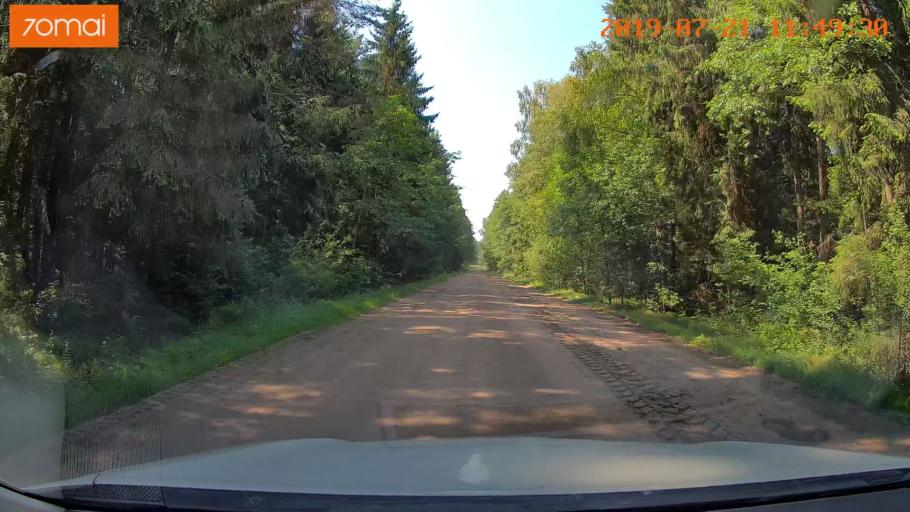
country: BY
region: Grodnenskaya
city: Lyubcha
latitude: 53.8921
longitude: 26.0381
